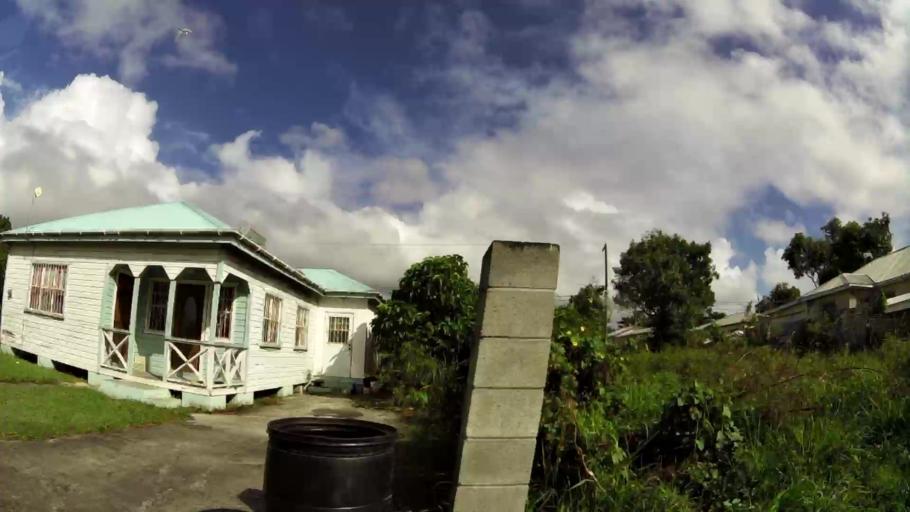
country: AG
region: Saint John
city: Saint John's
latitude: 17.1212
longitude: -61.8303
